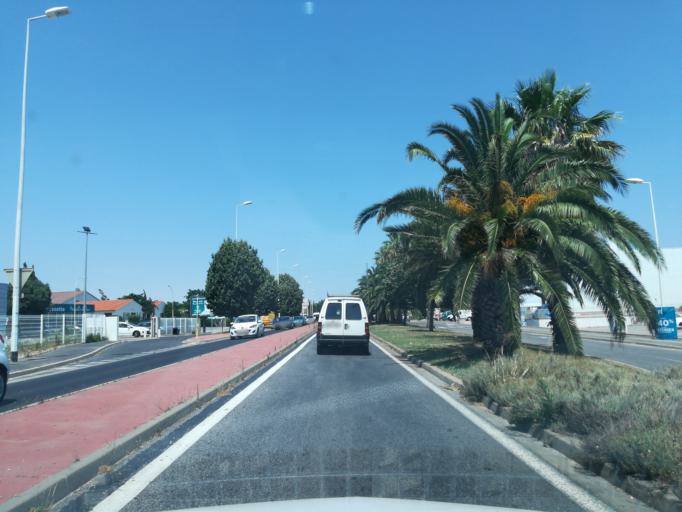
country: FR
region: Languedoc-Roussillon
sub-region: Departement des Pyrenees-Orientales
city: Perpignan
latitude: 42.6763
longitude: 2.8899
